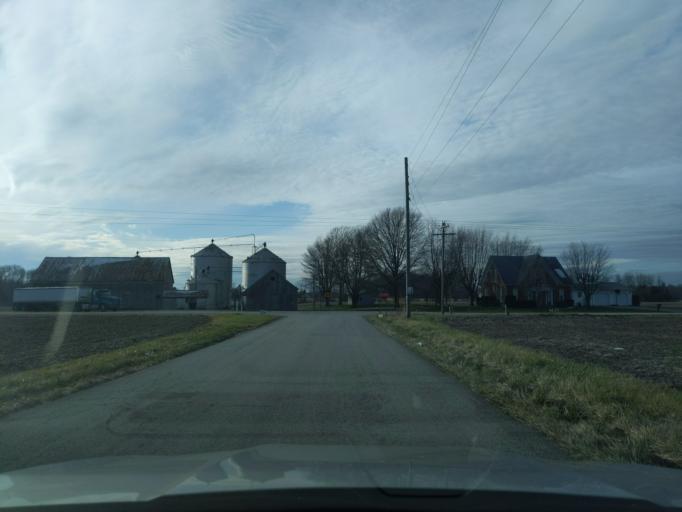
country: US
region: Indiana
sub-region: Decatur County
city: Westport
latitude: 39.2175
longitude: -85.4645
